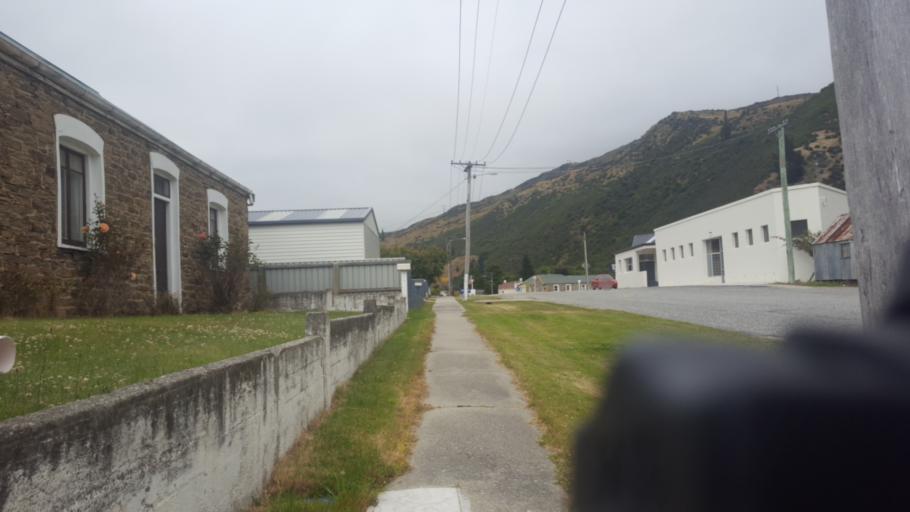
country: NZ
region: Otago
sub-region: Queenstown-Lakes District
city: Kingston
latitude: -45.5410
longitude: 169.3163
